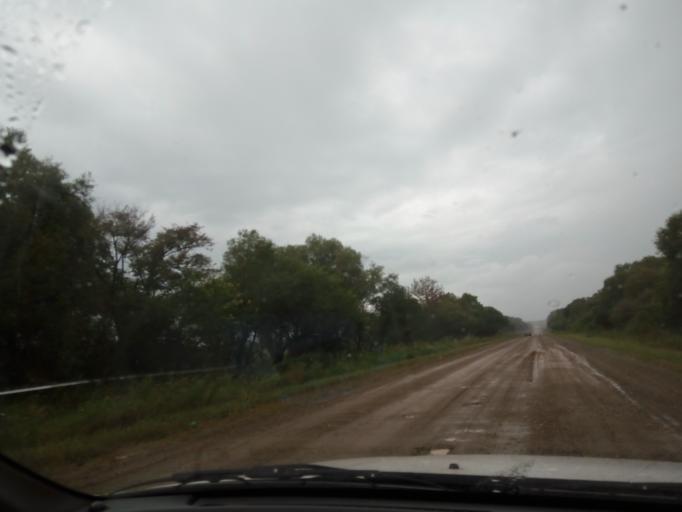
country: RU
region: Primorskiy
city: Lazo
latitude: 45.8442
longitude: 133.6445
